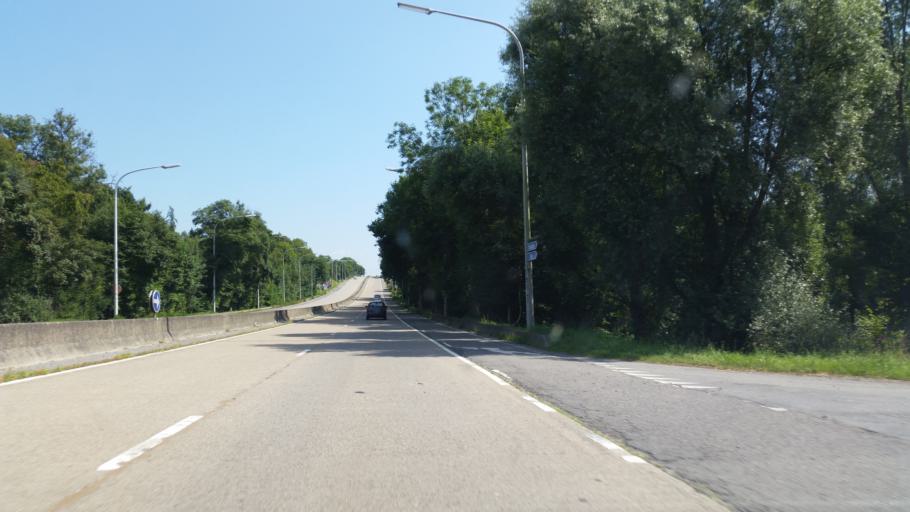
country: BE
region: Wallonia
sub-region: Province de Namur
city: Hamois
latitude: 50.2802
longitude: 5.2039
